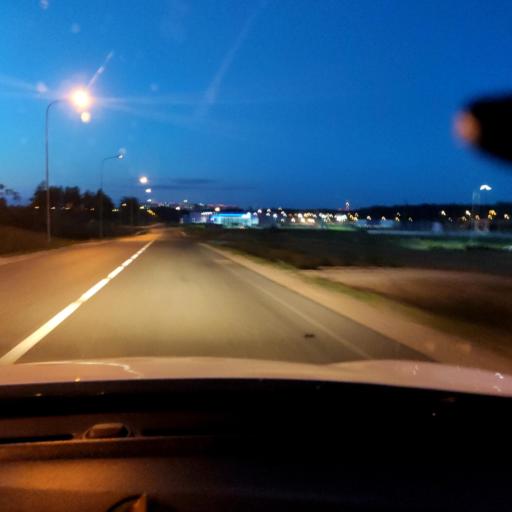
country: RU
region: Tatarstan
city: Osinovo
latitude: 55.8512
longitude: 48.8362
